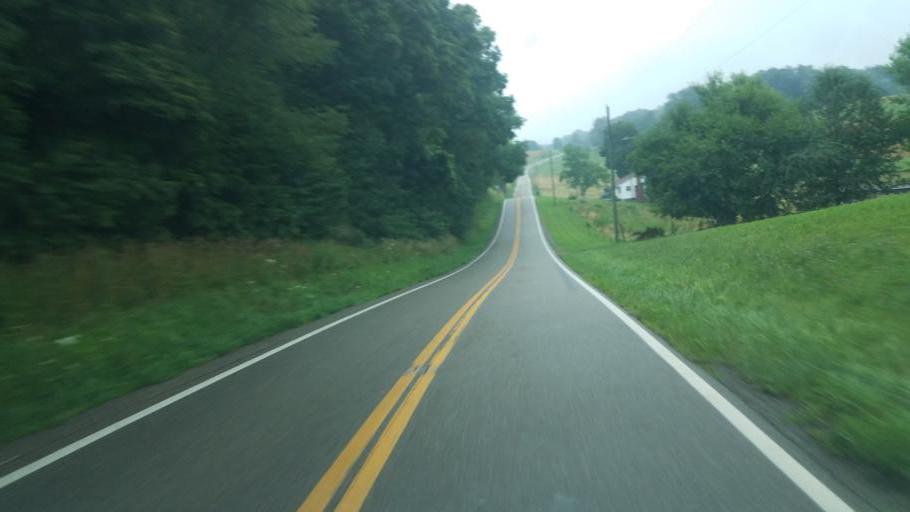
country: US
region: Ohio
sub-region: Carroll County
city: Carrollton
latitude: 40.4508
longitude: -81.1618
